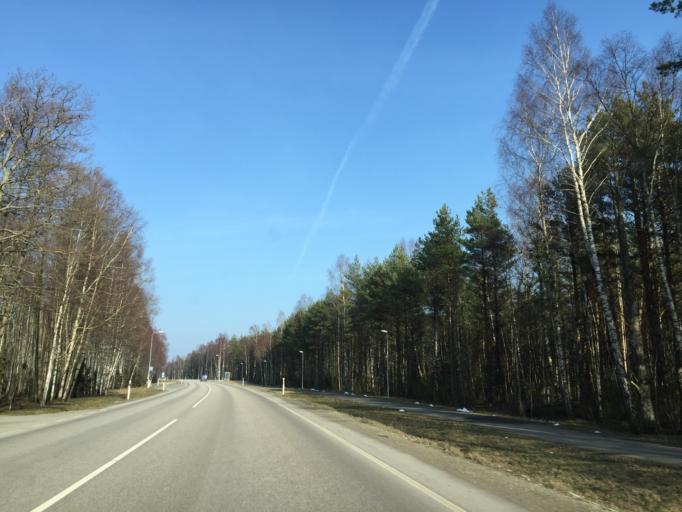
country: EE
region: Saare
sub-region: Kuressaare linn
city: Kuressaare
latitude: 58.2220
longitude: 22.3574
